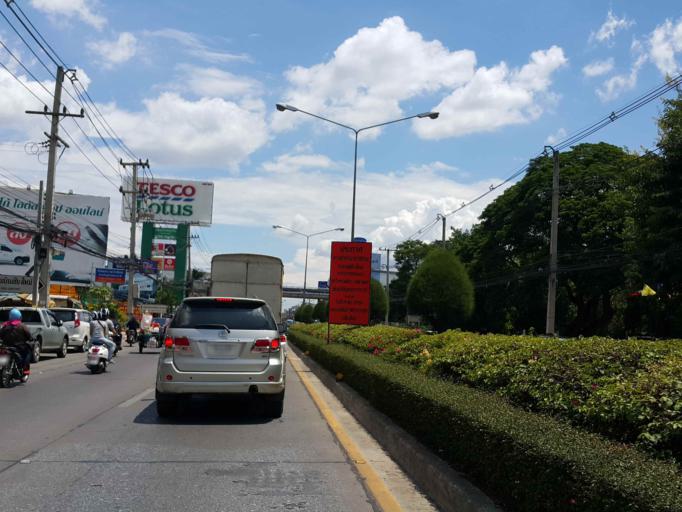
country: TH
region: Chiang Mai
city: Chiang Mai
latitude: 18.7606
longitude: 98.9716
